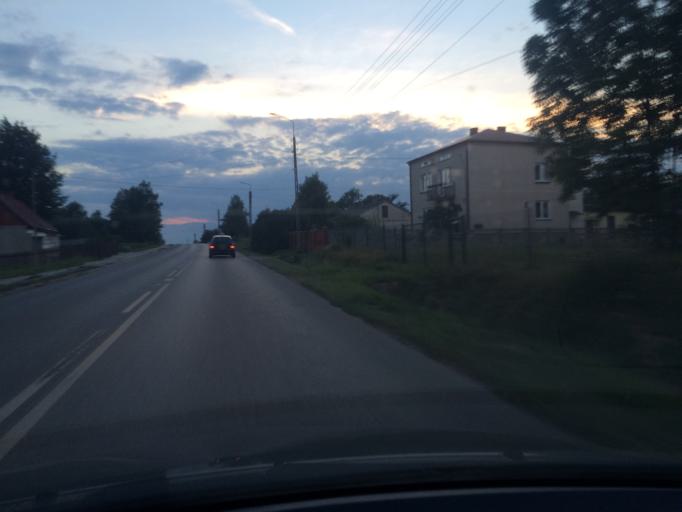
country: PL
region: Swietokrzyskie
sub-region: Powiat skarzyski
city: Suchedniow
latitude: 51.0456
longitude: 20.8796
